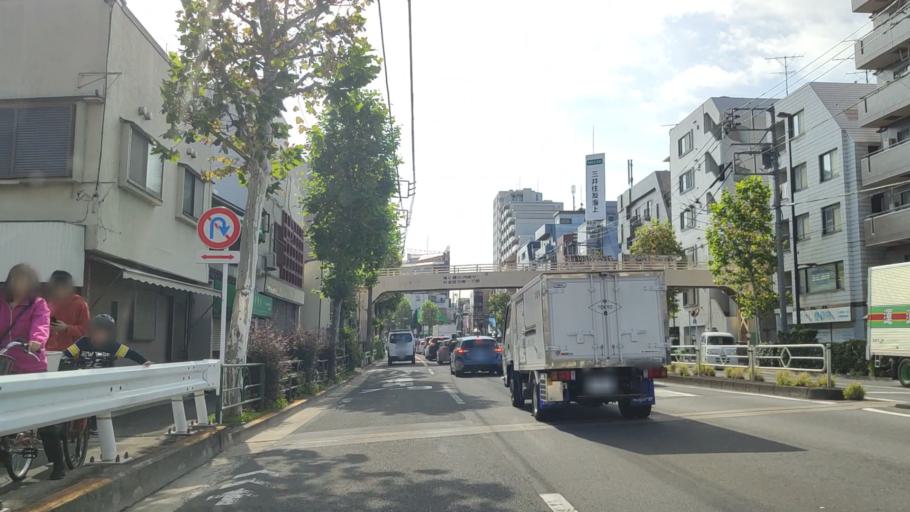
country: JP
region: Tokyo
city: Tokyo
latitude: 35.6803
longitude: 139.6572
